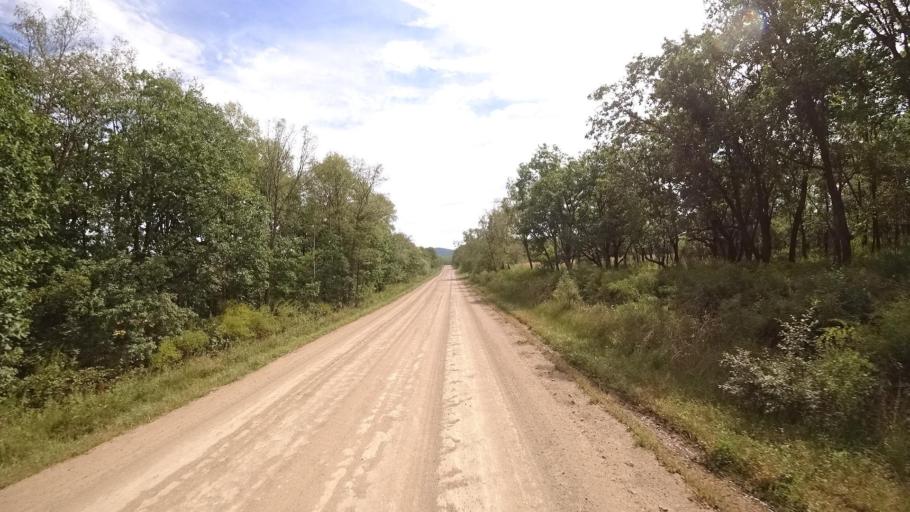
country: RU
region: Primorskiy
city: Yakovlevka
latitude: 44.6033
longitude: 133.6034
